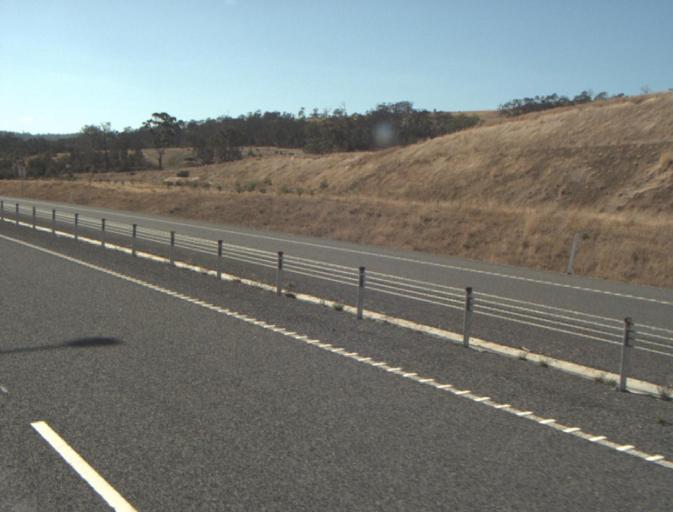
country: AU
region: Tasmania
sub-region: Launceston
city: Mayfield
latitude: -41.3550
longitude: 147.1043
